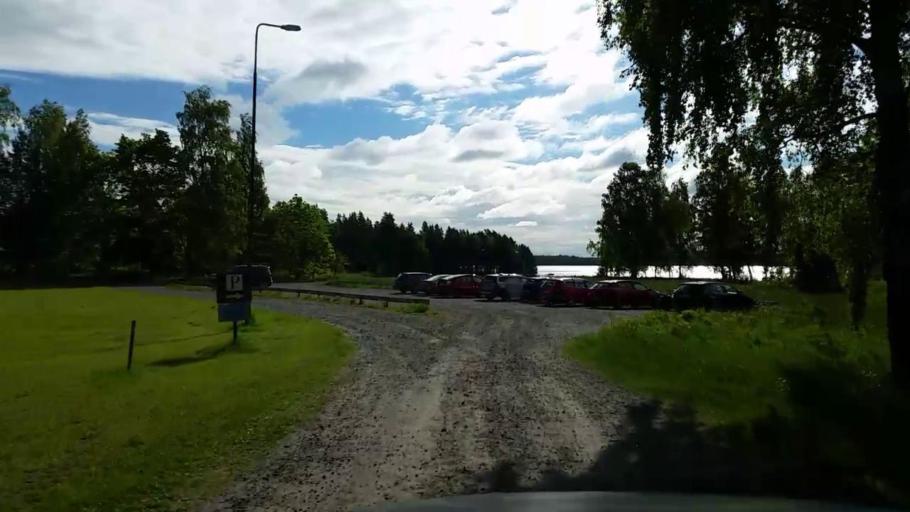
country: SE
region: Dalarna
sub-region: Borlange Kommun
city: Ornas
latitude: 60.5093
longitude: 15.6027
